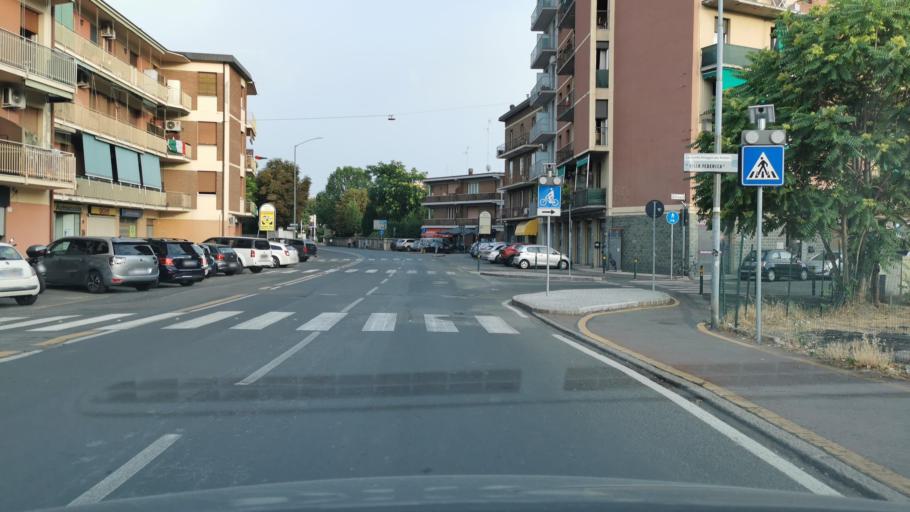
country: IT
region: Emilia-Romagna
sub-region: Provincia di Modena
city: Modena
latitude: 44.6357
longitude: 10.9345
